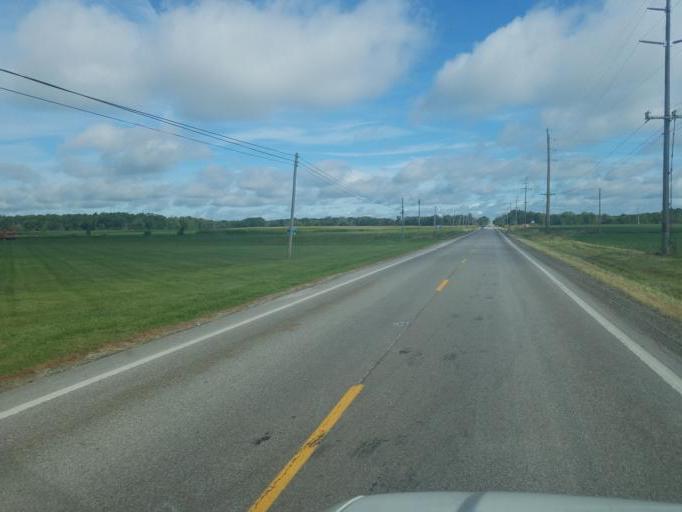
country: US
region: Ohio
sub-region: Wayne County
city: West Salem
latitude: 41.0302
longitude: -82.1262
